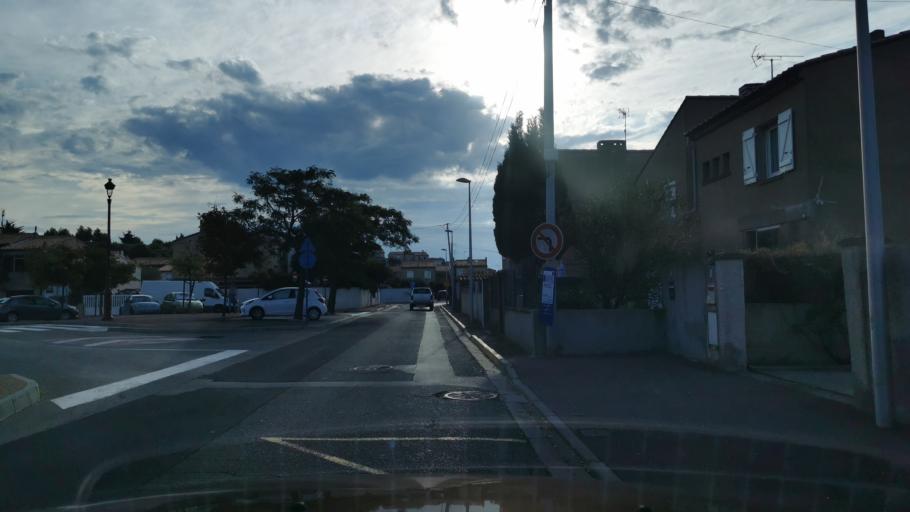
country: FR
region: Languedoc-Roussillon
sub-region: Departement de l'Aude
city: Gruissan
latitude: 43.1046
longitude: 3.0870
